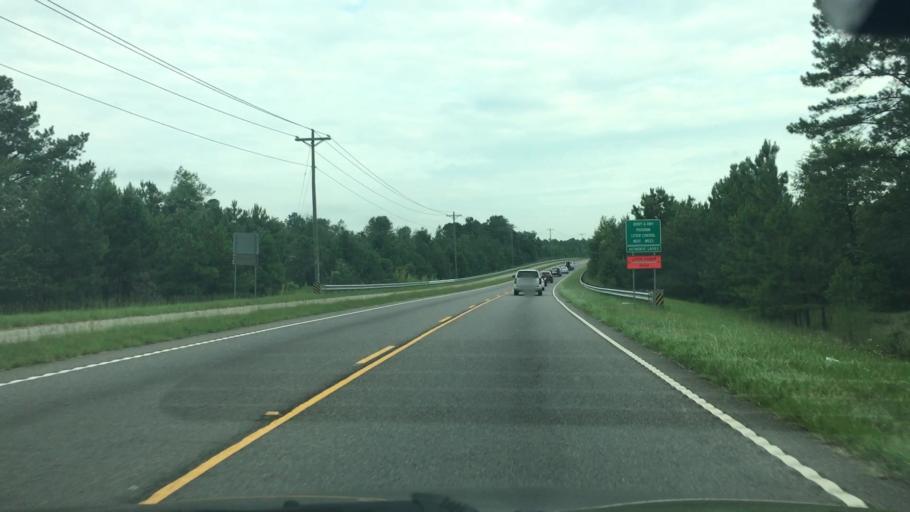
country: US
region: South Carolina
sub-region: Aiken County
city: Aiken
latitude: 33.5606
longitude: -81.6844
